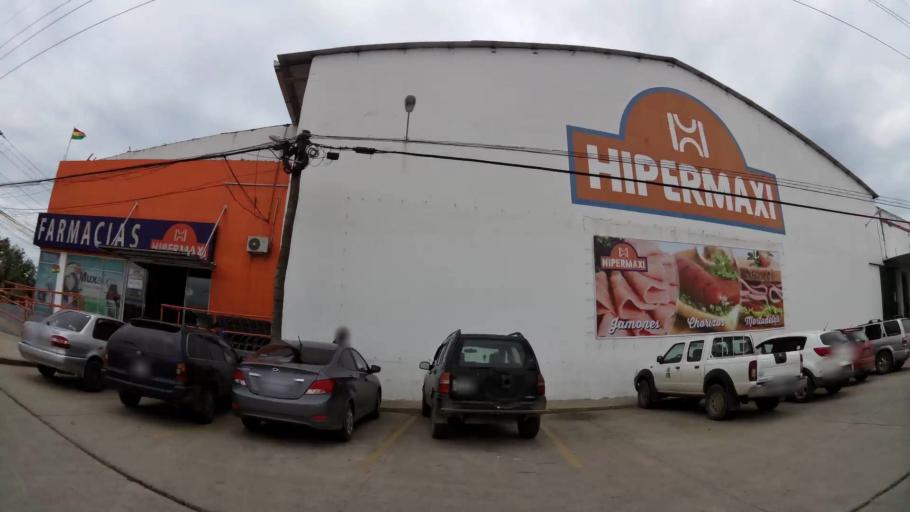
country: BO
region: Santa Cruz
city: Santa Cruz de la Sierra
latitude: -17.7498
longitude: -63.1851
